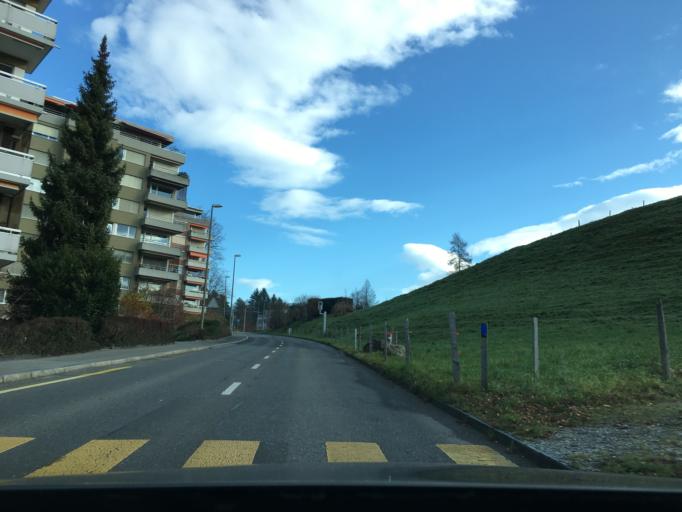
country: CH
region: Lucerne
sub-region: Lucerne-Land District
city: Adligenswil
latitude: 47.0522
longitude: 8.3459
